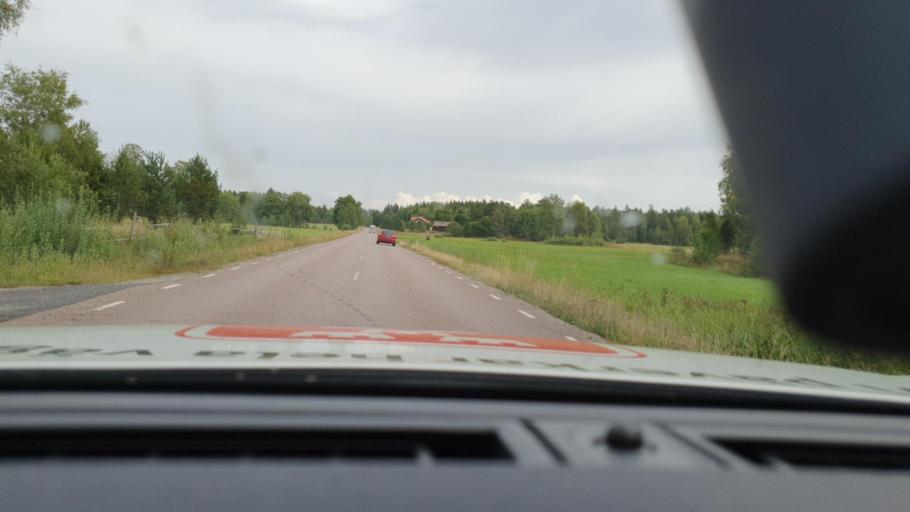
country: SE
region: Uppsala
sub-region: Heby Kommun
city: OEstervala
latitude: 60.0924
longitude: 17.0967
